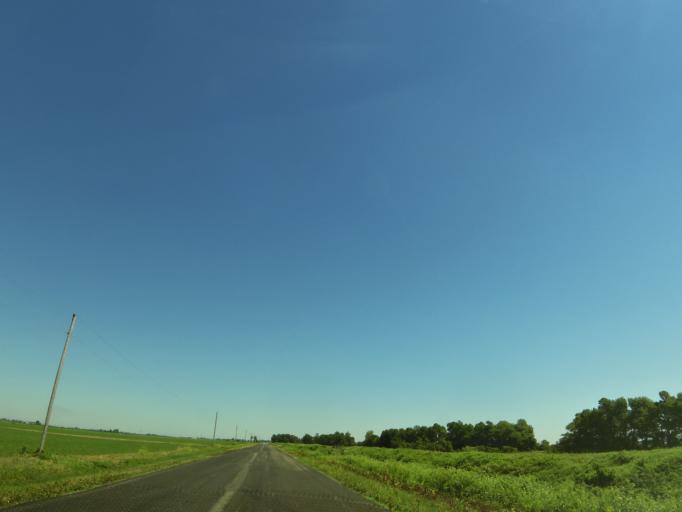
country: US
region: Missouri
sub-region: New Madrid County
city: Lilbourn
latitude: 36.5588
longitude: -89.7035
